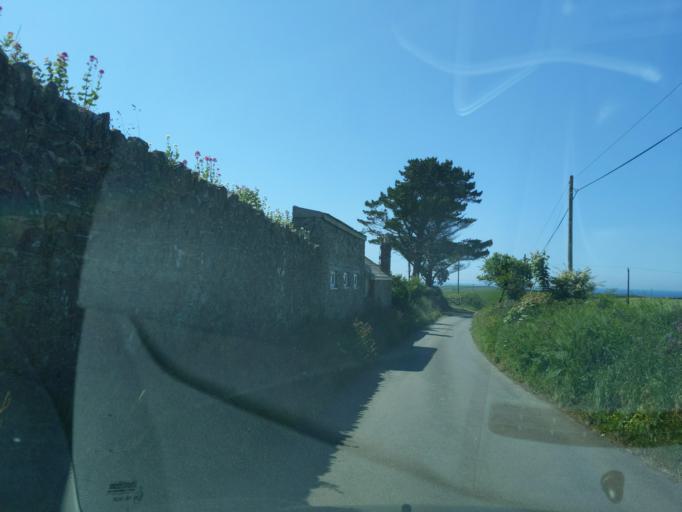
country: GB
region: England
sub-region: Cornwall
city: Wadebridge
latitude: 50.5828
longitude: -4.8419
